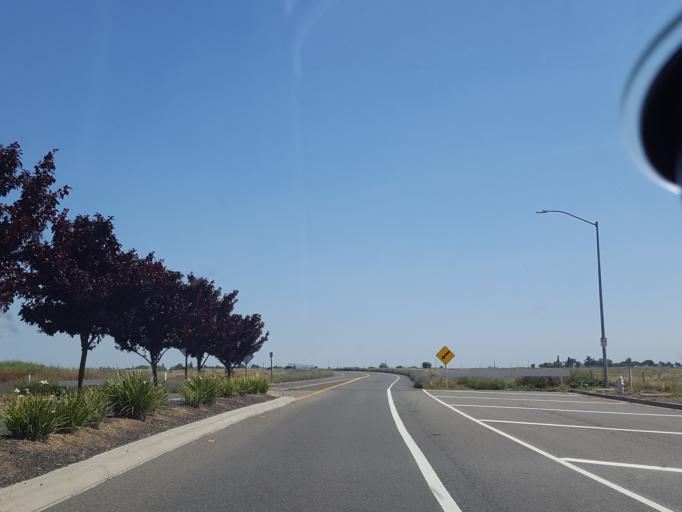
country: US
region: California
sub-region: Sacramento County
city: Rancho Cordova
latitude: 38.5685
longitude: -121.2667
